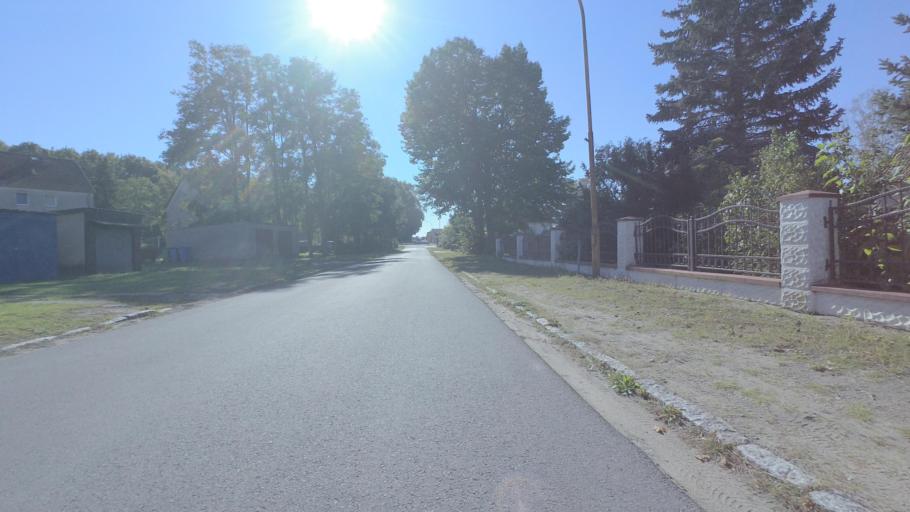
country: DE
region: Brandenburg
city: Sperenberg
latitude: 52.1452
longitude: 13.3669
